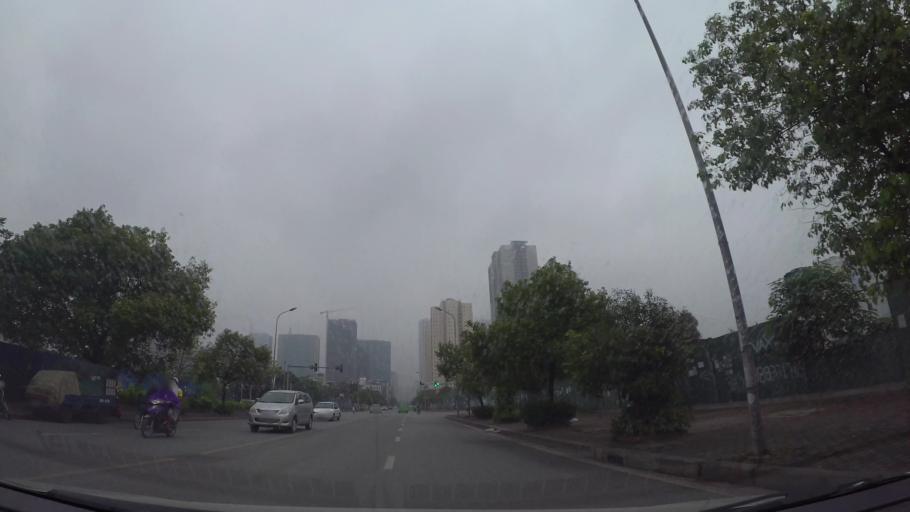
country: VN
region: Ha Noi
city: Thanh Xuan
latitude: 21.0124
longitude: 105.7920
